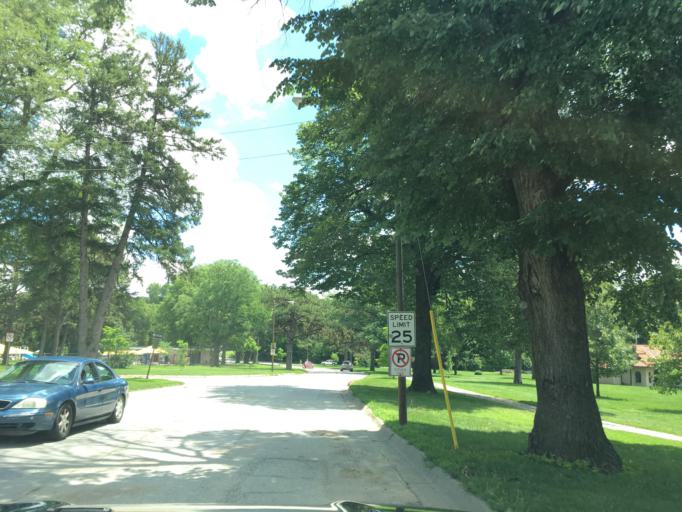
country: US
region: Nebraska
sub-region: Douglas County
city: Ralston
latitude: 41.2560
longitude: -96.0077
